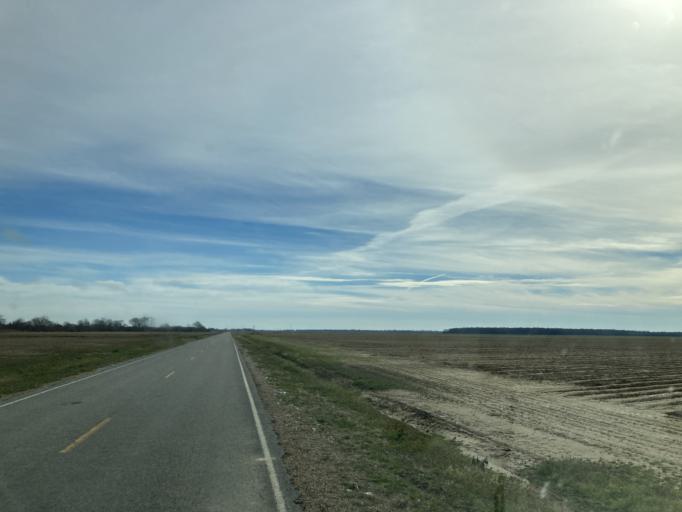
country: US
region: Mississippi
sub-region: Humphreys County
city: Belzoni
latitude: 33.0625
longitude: -90.6148
